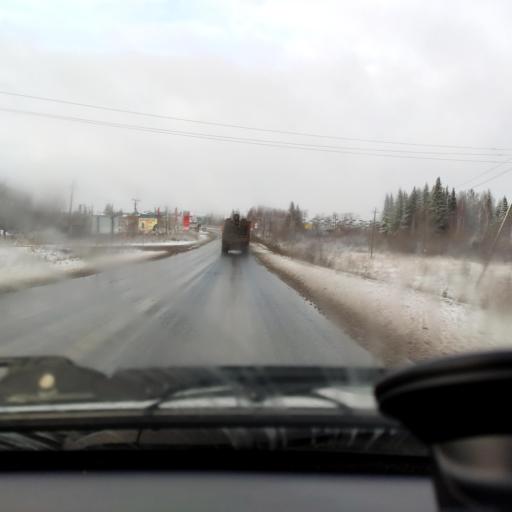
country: RU
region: Perm
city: Nytva
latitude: 57.9473
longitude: 55.3611
